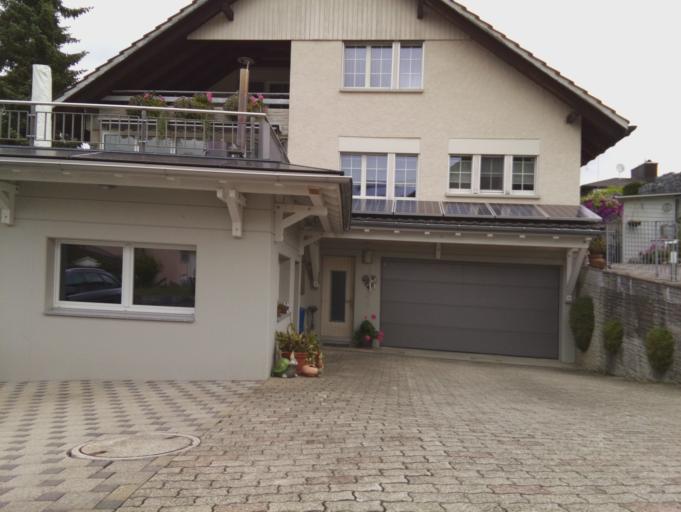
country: CH
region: Saint Gallen
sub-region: Wahlkreis Toggenburg
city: Ganterschwil
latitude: 47.3834
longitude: 9.0938
